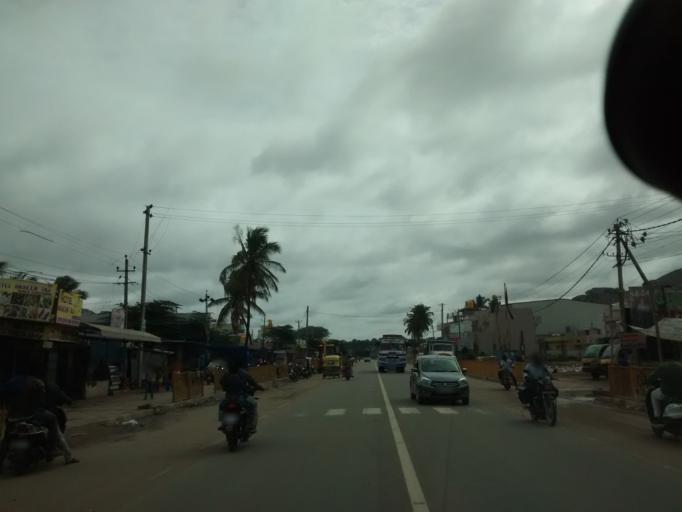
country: IN
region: Karnataka
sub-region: Tumkur
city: Tumkur
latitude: 13.3852
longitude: 77.1173
